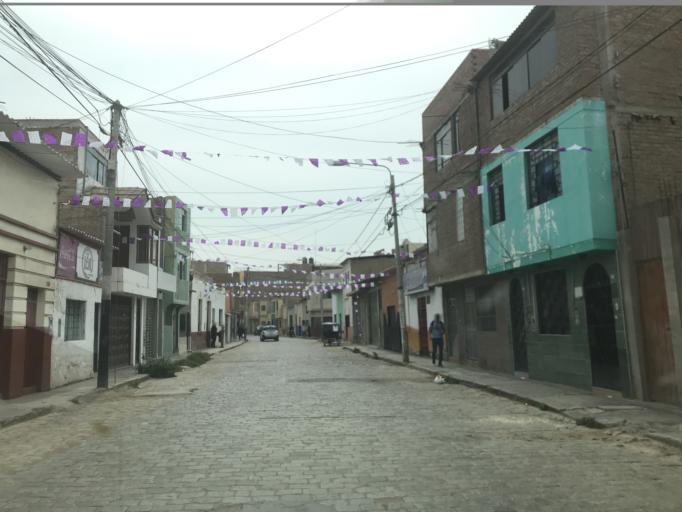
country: PE
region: Lambayeque
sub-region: Provincia de Chiclayo
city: Santa Rosa
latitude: -6.7719
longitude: -79.8328
